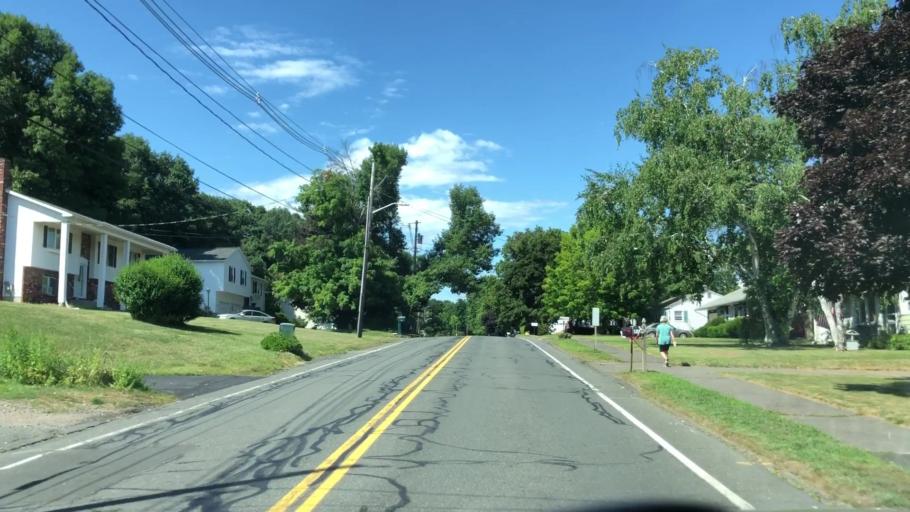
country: US
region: Massachusetts
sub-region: Hampden County
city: Holyoke
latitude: 42.1907
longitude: -72.6490
